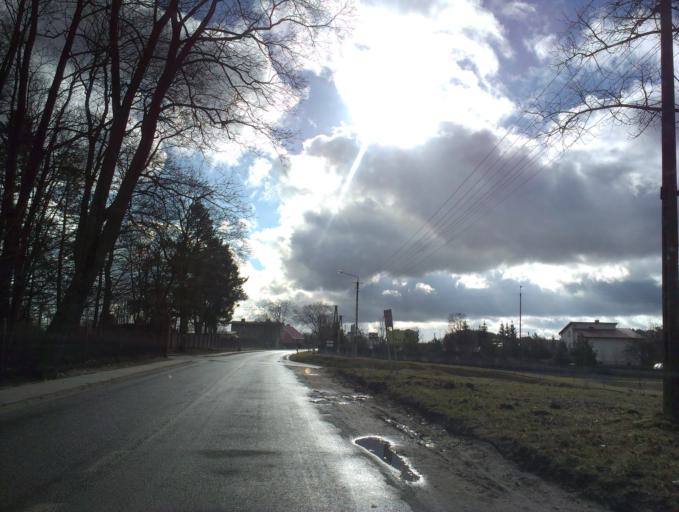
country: PL
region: Pomeranian Voivodeship
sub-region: Powiat czluchowski
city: Rzeczenica
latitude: 53.6493
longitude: 17.1445
